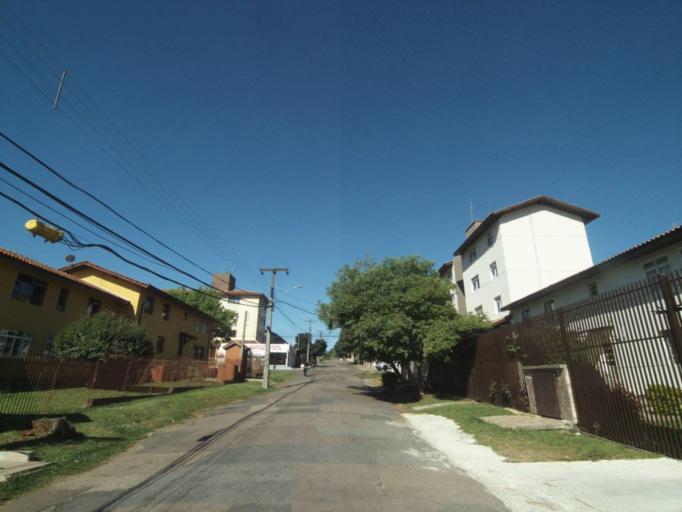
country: BR
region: Parana
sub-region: Curitiba
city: Curitiba
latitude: -25.4540
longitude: -49.3536
